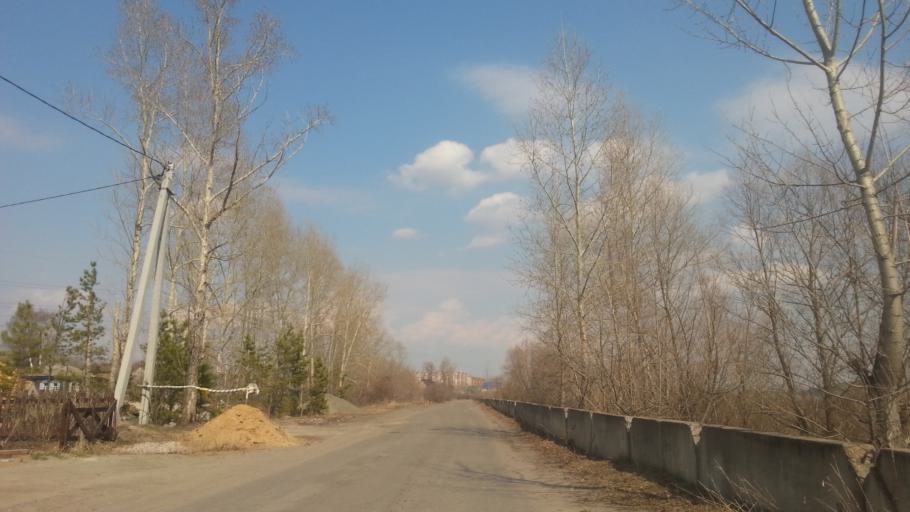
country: RU
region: Altai Krai
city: Yuzhnyy
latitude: 53.3099
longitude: 83.7228
